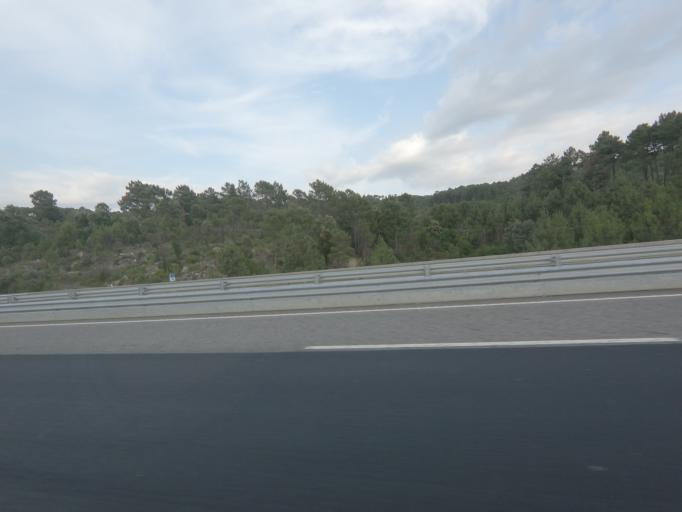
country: PT
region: Vila Real
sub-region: Boticas
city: Boticas
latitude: 41.6199
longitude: -7.6045
